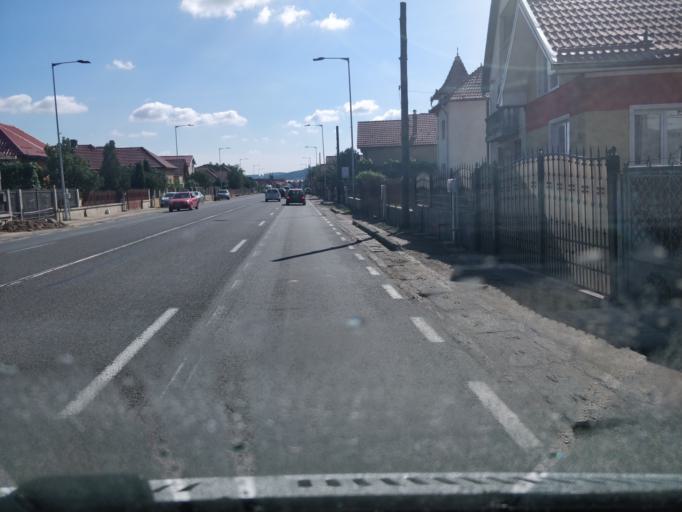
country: RO
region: Cluj
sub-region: Comuna Floresti
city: Floresti
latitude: 46.7440
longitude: 23.4702
